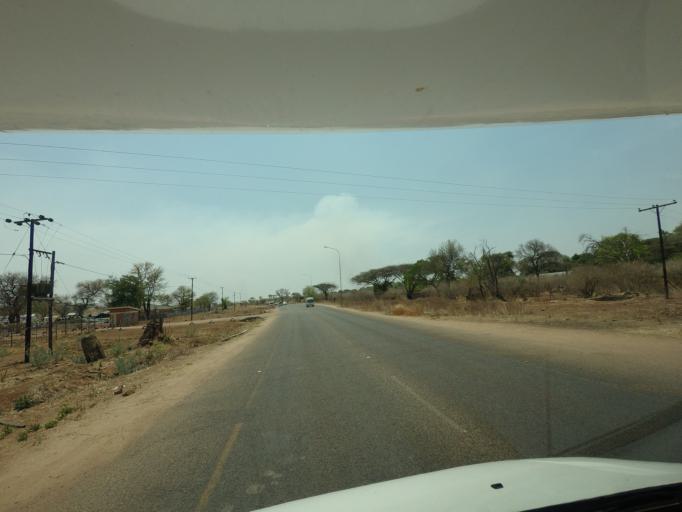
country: BW
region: North West
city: Kasane
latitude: -17.7862
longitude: 25.1801
